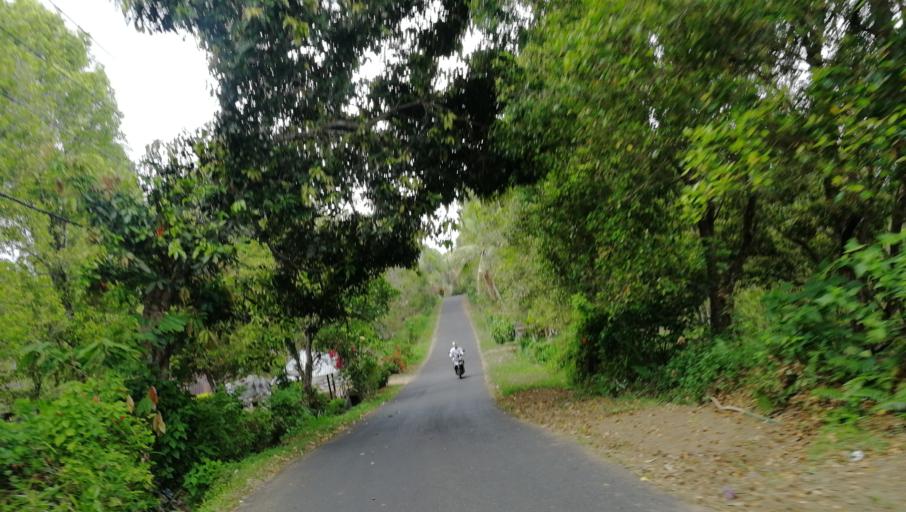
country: ID
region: Bali
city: Puspajati
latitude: -8.2784
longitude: 115.0291
